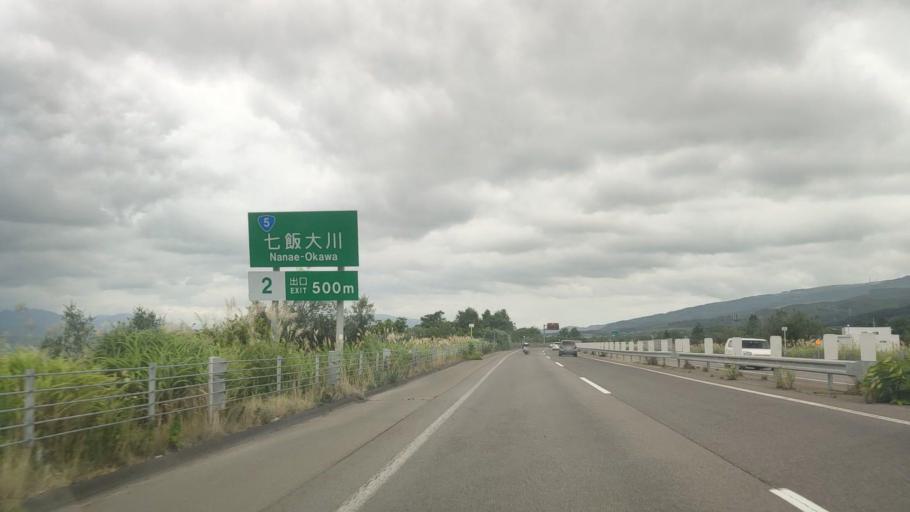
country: JP
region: Hokkaido
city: Nanae
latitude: 41.8614
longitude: 140.7328
